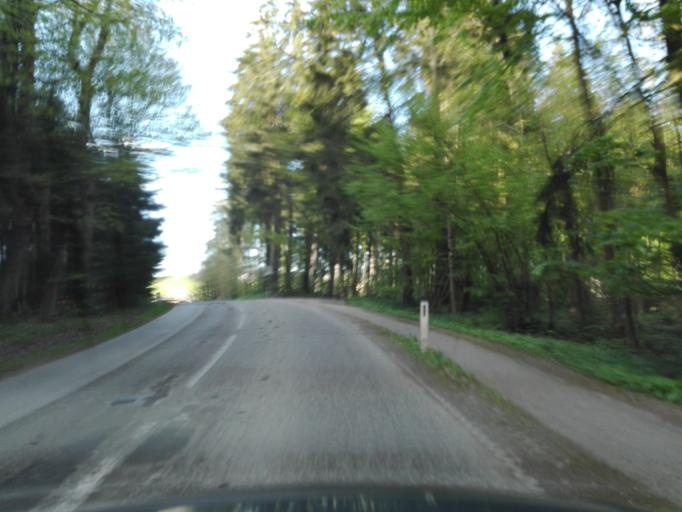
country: AT
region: Upper Austria
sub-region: Politischer Bezirk Rohrbach
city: Kleinzell im Muehlkreis
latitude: 48.4791
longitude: 13.9623
